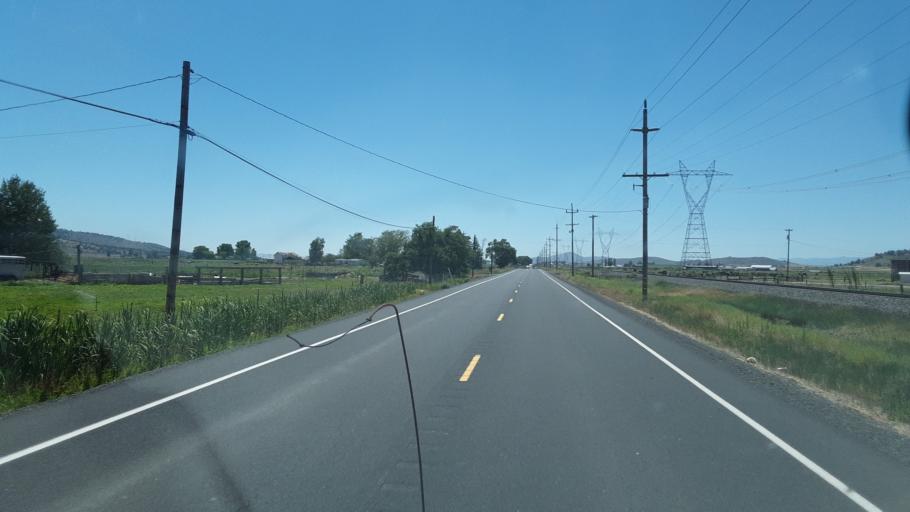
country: US
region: Oregon
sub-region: Klamath County
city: Altamont
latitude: 42.0946
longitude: -121.6901
